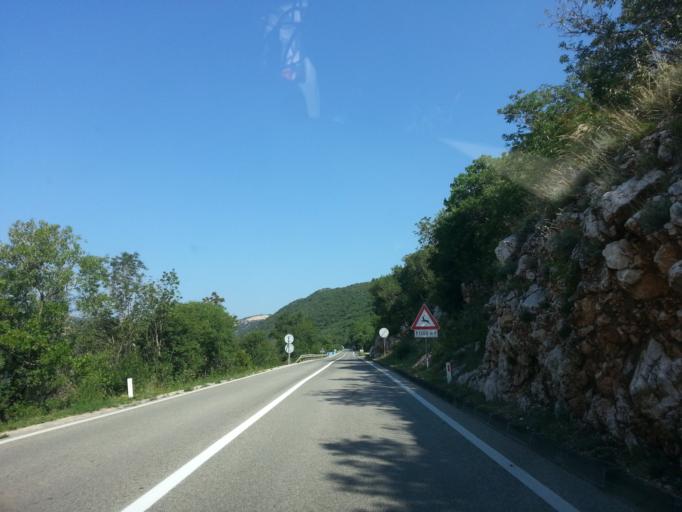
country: HR
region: Primorsko-Goranska
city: Krasica
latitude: 45.2934
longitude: 14.5659
